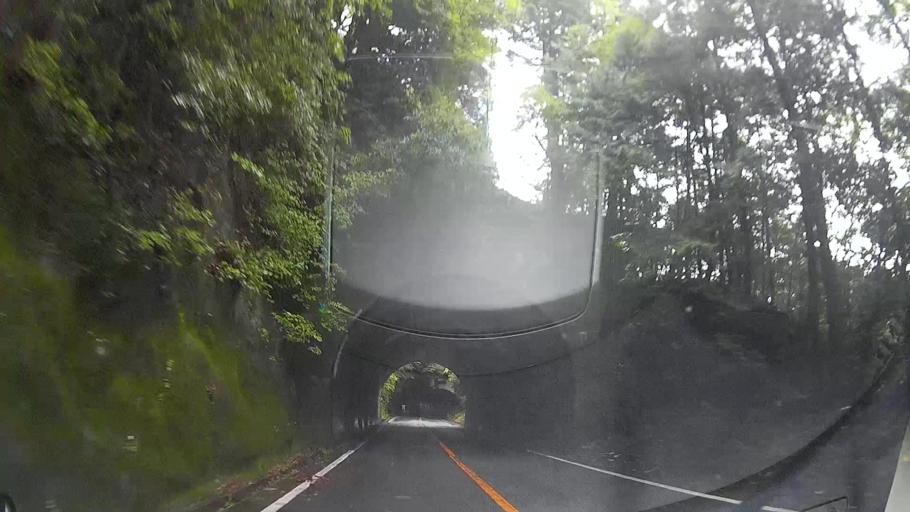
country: JP
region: Oita
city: Hita
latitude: 33.1823
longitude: 131.0010
